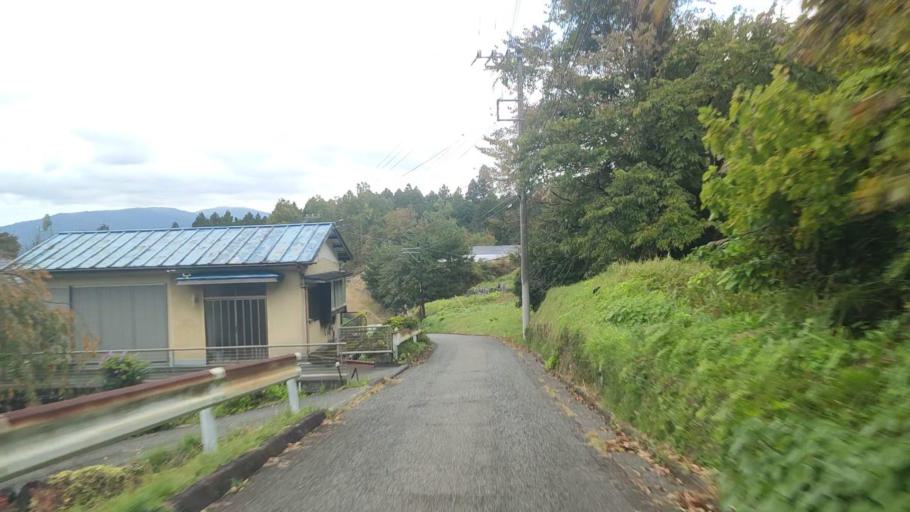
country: JP
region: Shizuoka
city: Ito
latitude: 34.8924
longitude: 138.9462
